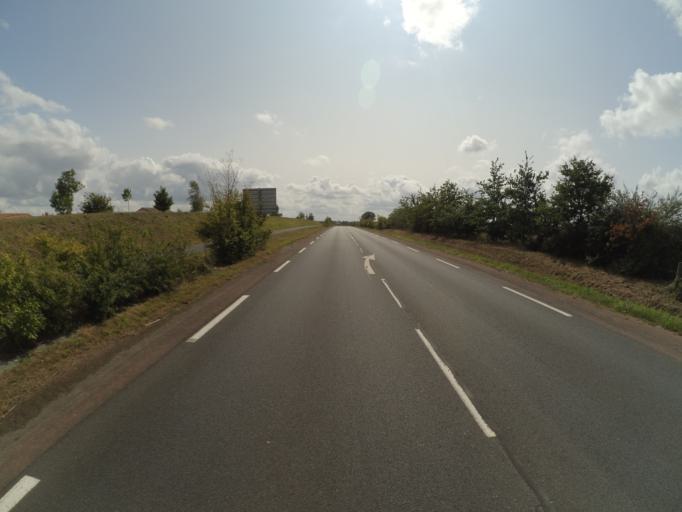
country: FR
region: Pays de la Loire
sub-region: Departement de la Vendee
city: La Bruffiere
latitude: 47.0191
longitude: -1.2035
